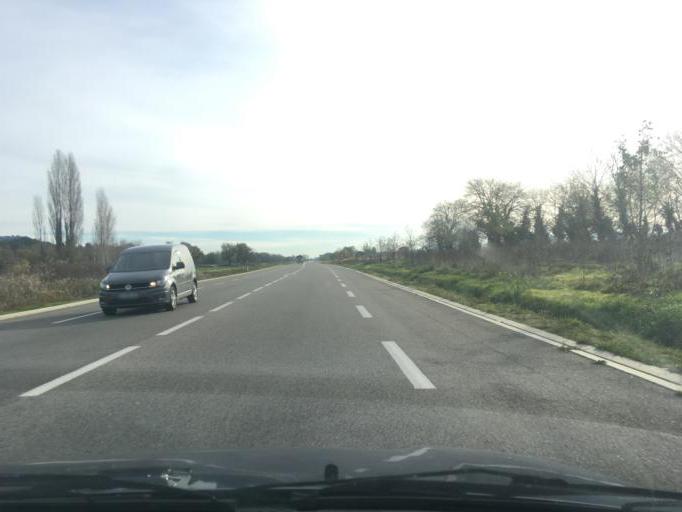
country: FR
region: Provence-Alpes-Cote d'Azur
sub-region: Departement du Vaucluse
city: Cadenet
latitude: 43.7217
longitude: 5.3875
